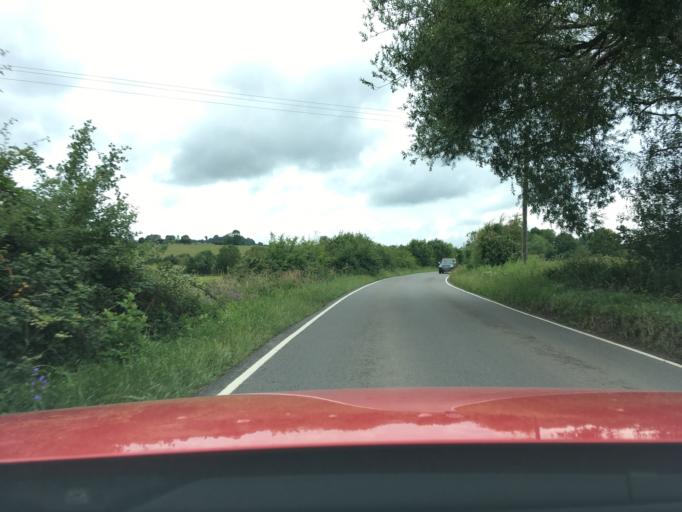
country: GB
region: England
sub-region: Warwickshire
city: Shipston on Stour
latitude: 52.0926
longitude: -1.6805
